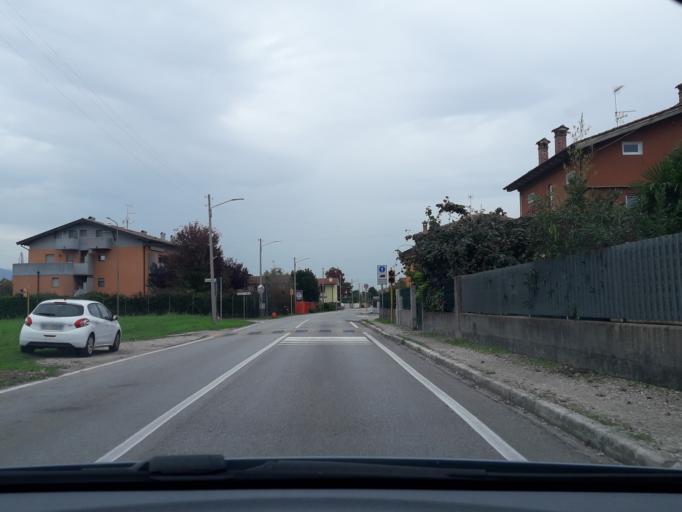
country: IT
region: Friuli Venezia Giulia
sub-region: Provincia di Udine
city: Udine
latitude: 46.0880
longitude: 13.2575
